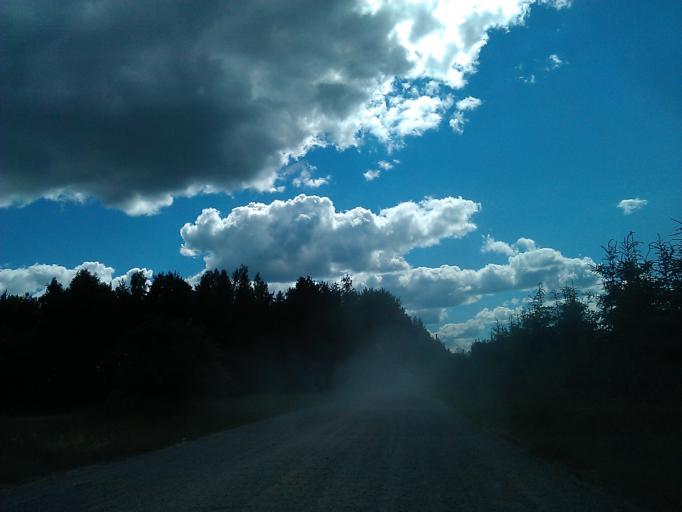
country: LV
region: Vilanu
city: Vilani
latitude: 56.5878
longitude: 26.9509
